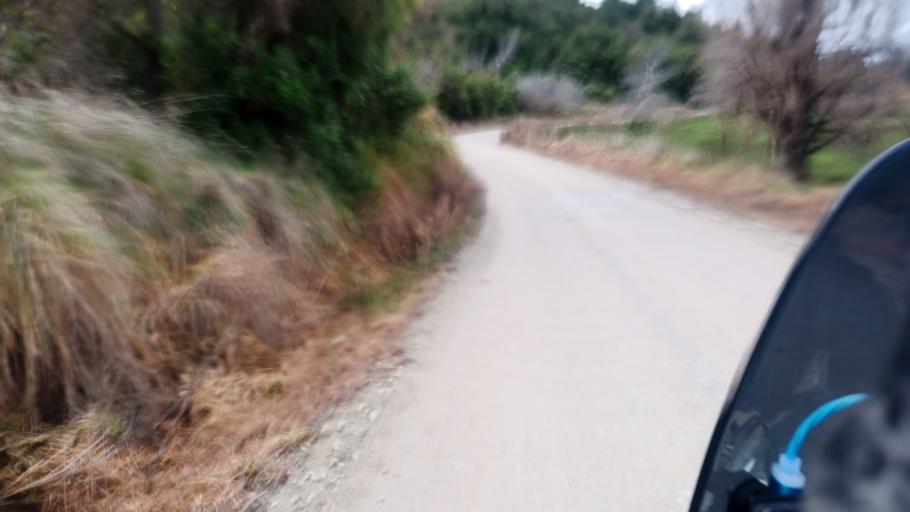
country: NZ
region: Gisborne
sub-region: Gisborne District
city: Gisborne
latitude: -38.3831
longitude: 177.9587
